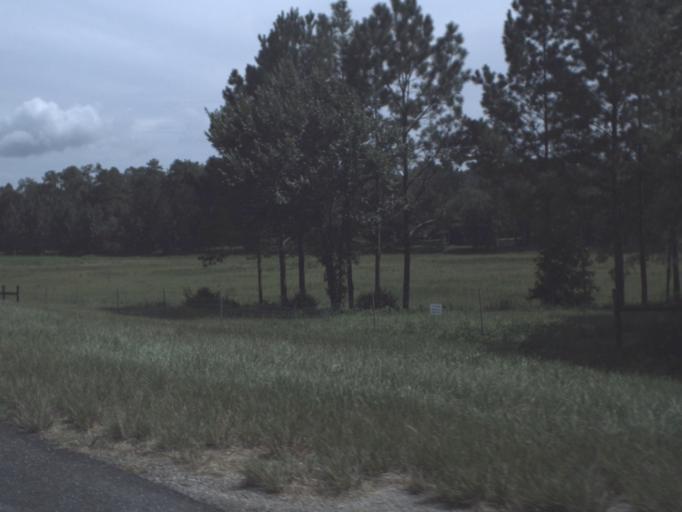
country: US
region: Florida
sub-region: Hernando County
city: Hill 'n Dale
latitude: 28.5255
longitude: -82.3141
